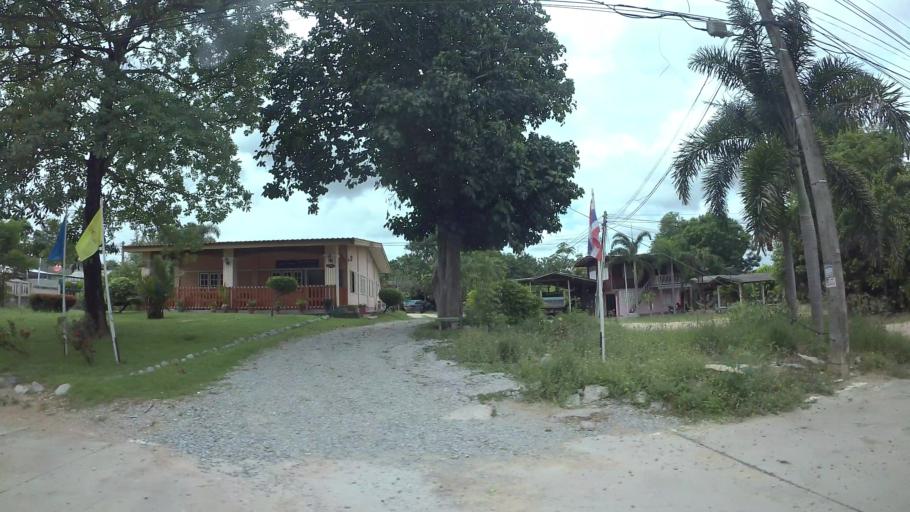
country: TH
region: Chon Buri
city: Si Racha
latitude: 13.1617
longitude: 100.9755
